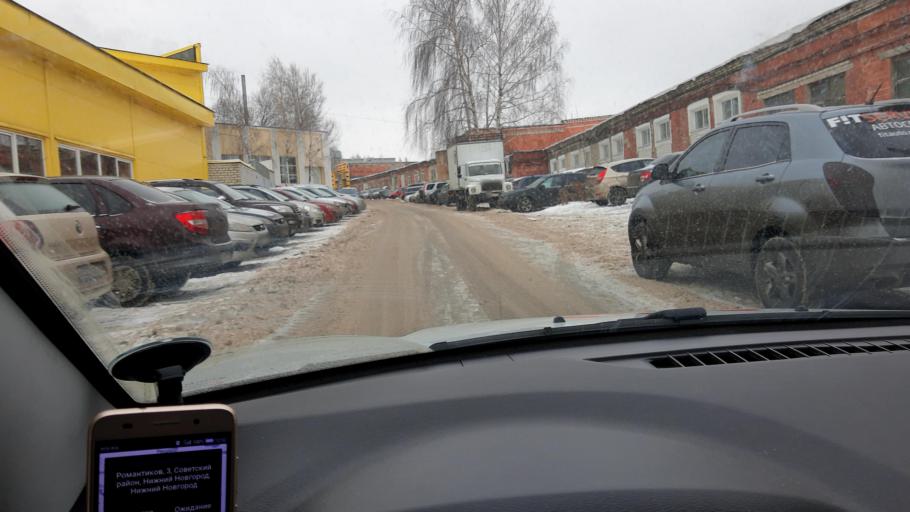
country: RU
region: Nizjnij Novgorod
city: Nizhniy Novgorod
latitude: 56.2473
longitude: 43.9614
